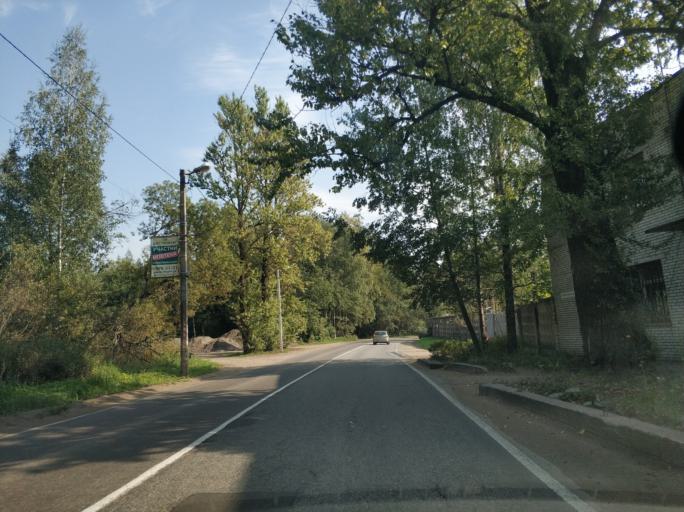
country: RU
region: Leningrad
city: Yanino Vtoroye
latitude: 60.0130
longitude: 30.5894
